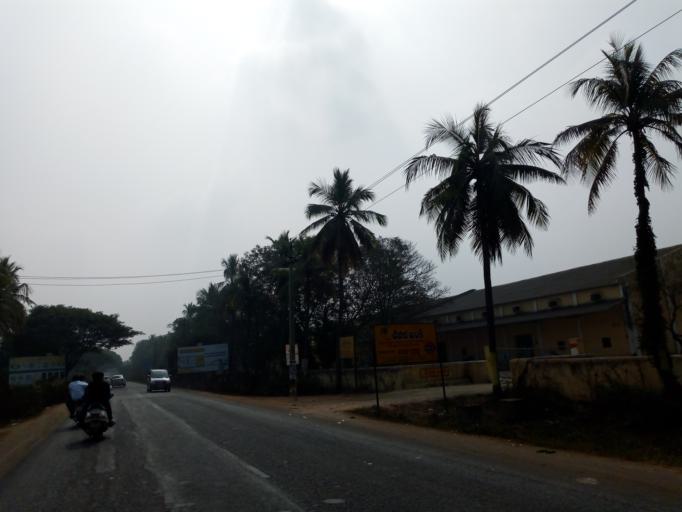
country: IN
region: Andhra Pradesh
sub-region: West Godavari
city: Bhimavaram
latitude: 16.5769
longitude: 81.4792
